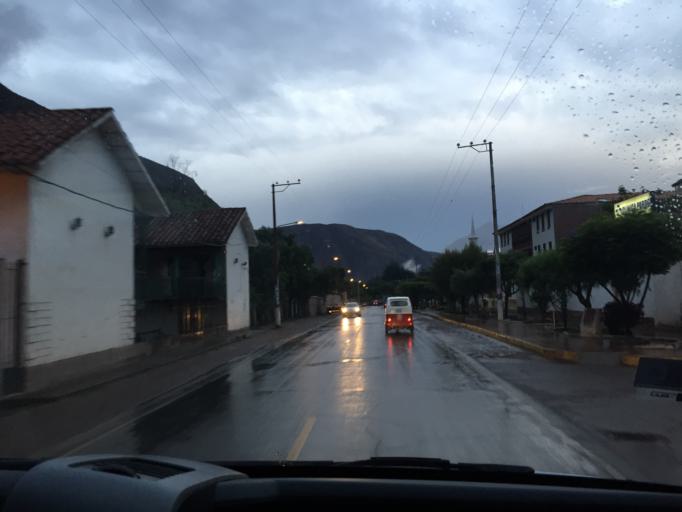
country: PE
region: Cusco
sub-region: Provincia de Urubamba
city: Urubamba
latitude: -13.3090
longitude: -72.1161
